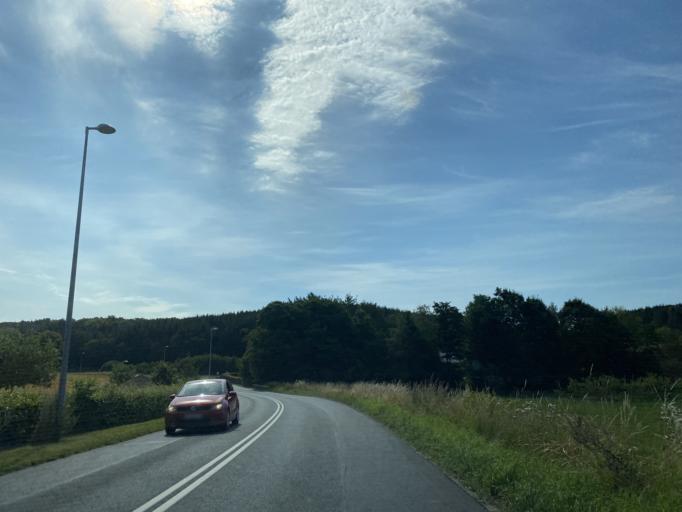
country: DK
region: Central Jutland
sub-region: Favrskov Kommune
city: Hammel
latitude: 56.2656
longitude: 9.8362
